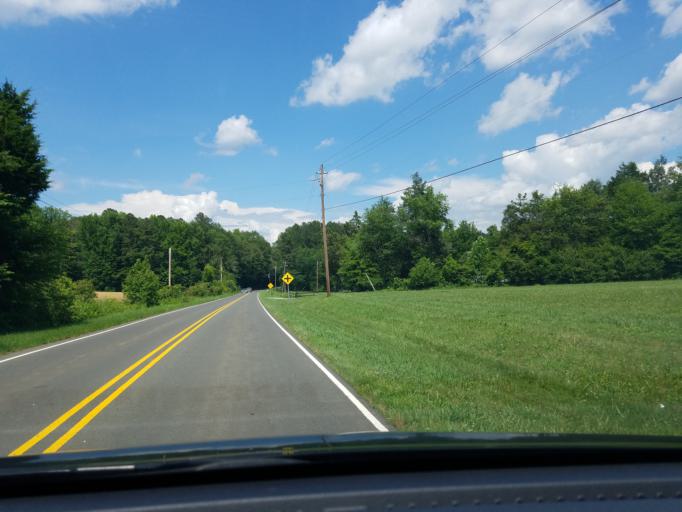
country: US
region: North Carolina
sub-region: Durham County
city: Gorman
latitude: 36.1550
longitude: -78.8980
